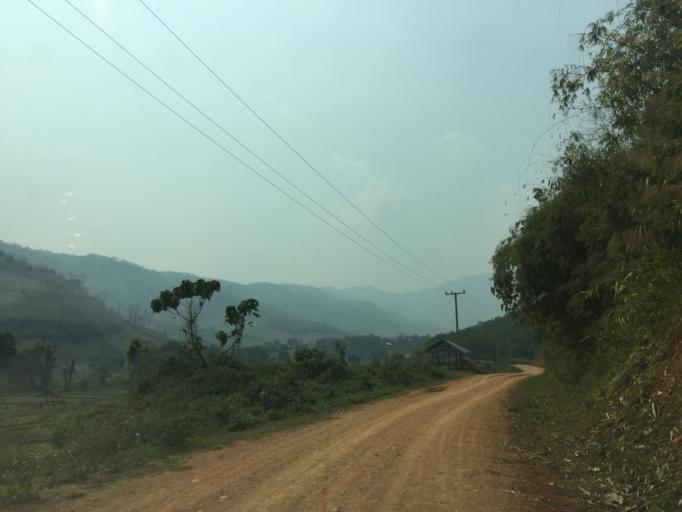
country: TH
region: Phayao
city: Phu Sang
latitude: 19.5753
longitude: 100.5257
